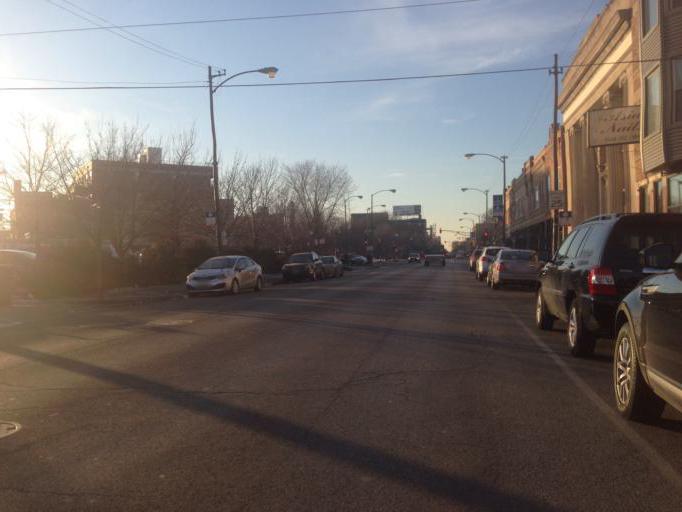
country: US
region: Illinois
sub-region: Cook County
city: Lincolnwood
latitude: 41.9275
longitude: -87.7047
